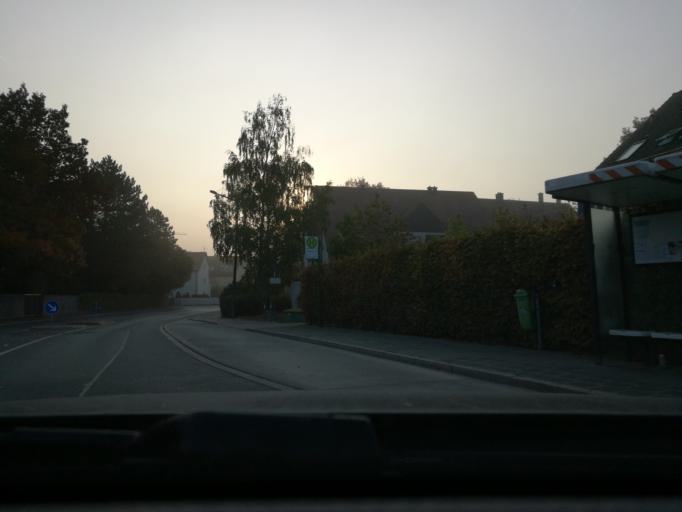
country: DE
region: Bavaria
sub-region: Regierungsbezirk Mittelfranken
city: Furth
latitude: 49.4883
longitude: 10.9578
